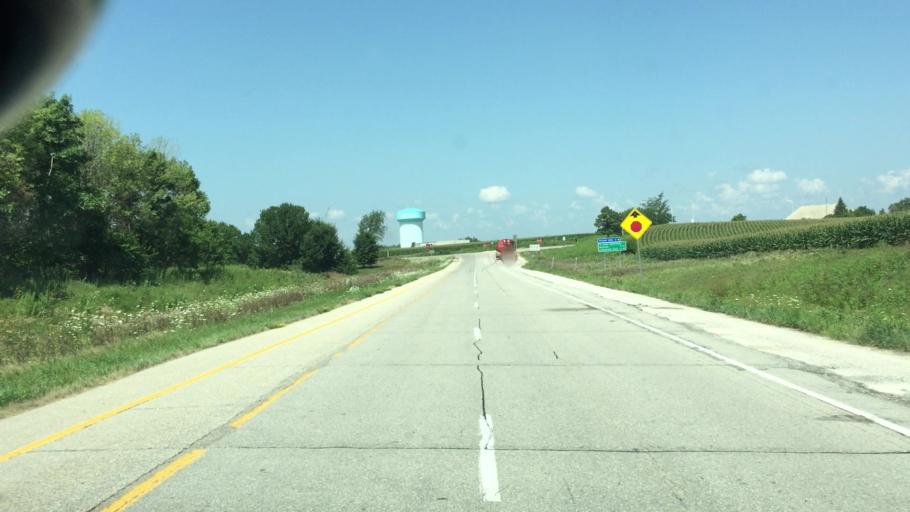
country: US
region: Iowa
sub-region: Jasper County
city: Newton
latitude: 41.6834
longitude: -92.9973
